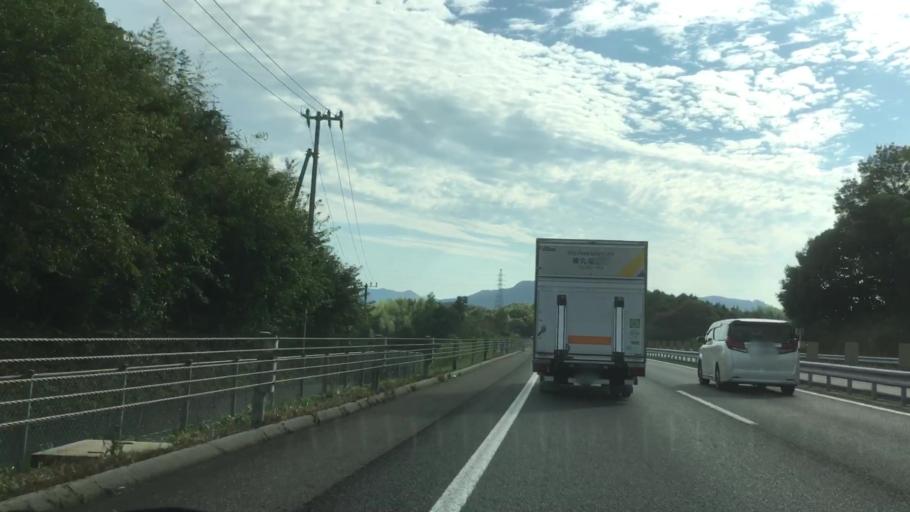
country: JP
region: Yamaguchi
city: Yanai
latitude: 34.0947
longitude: 132.0973
